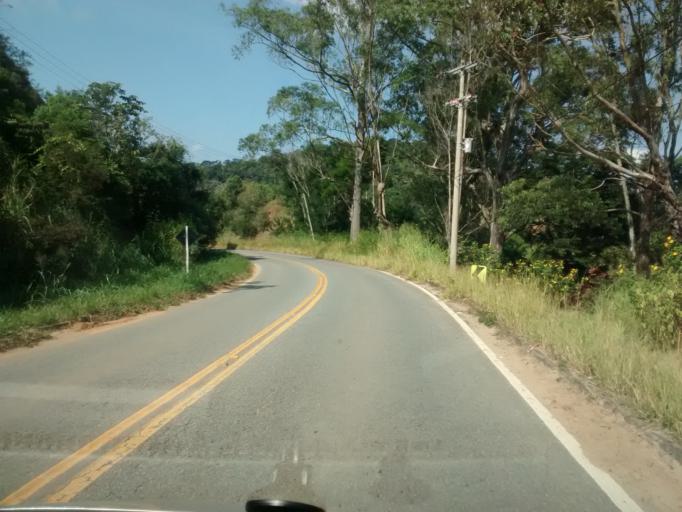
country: BR
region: Rio de Janeiro
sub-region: Miguel Pereira
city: Miguel Pereira
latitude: -22.4728
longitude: -43.5479
